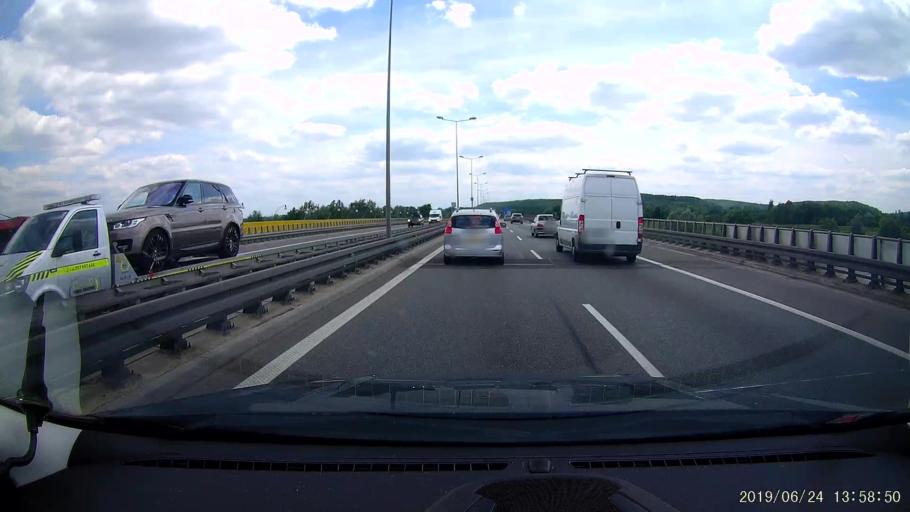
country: PL
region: Lesser Poland Voivodeship
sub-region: Powiat krakowski
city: Piekary
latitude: 50.0310
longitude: 19.8183
